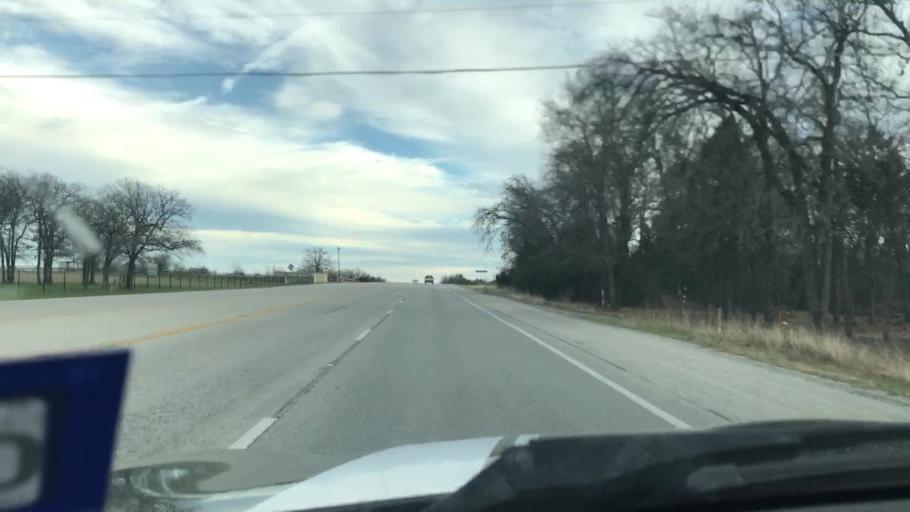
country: US
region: Texas
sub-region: Bastrop County
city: Camp Swift
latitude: 30.2902
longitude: -97.2527
